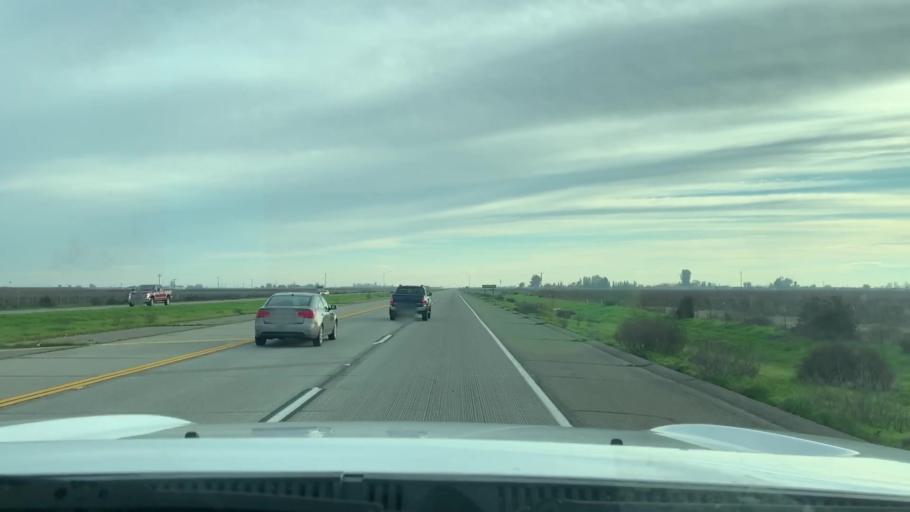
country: US
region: California
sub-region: Fresno County
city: Caruthers
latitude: 36.5662
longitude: -119.7863
